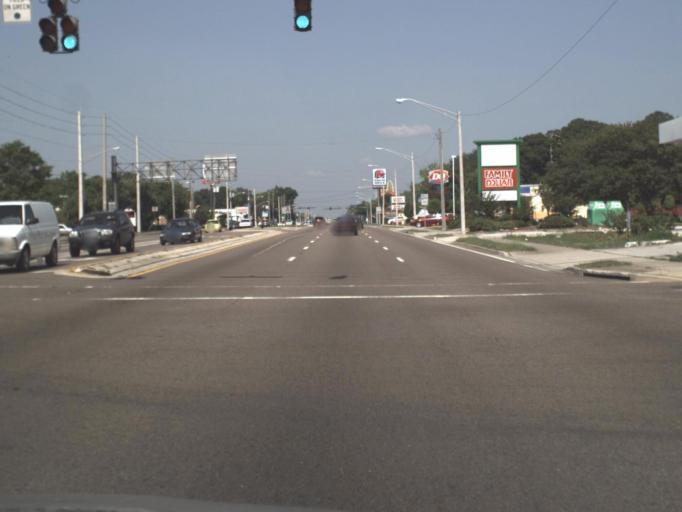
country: US
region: Florida
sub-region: Clay County
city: Bellair-Meadowbrook Terrace
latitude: 30.2484
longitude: -81.7644
